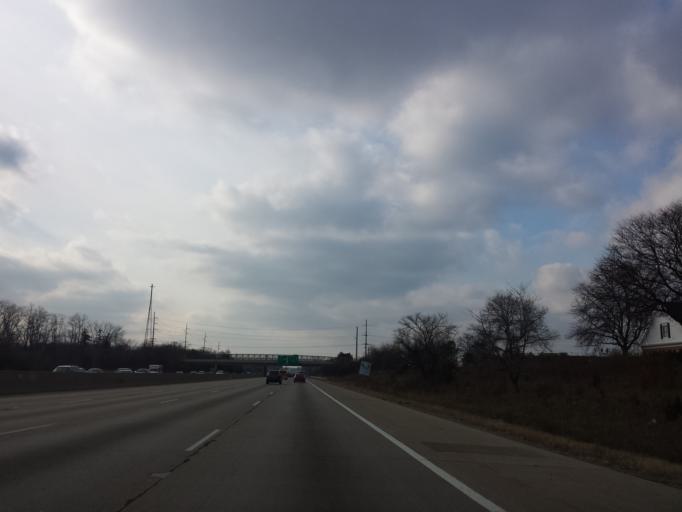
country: US
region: Michigan
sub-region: Oakland County
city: Farmington Hills
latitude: 42.4955
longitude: -83.3746
